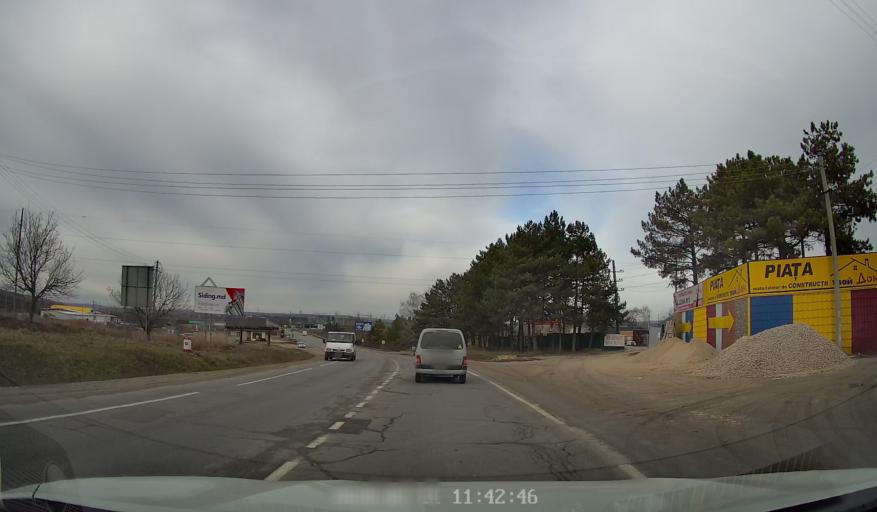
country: MD
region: Balti
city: Balti
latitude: 47.7918
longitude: 27.8816
